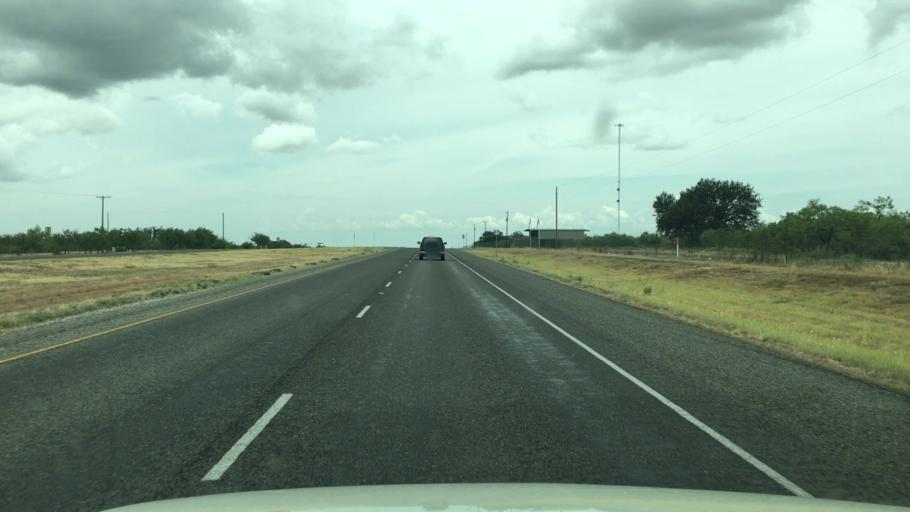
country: US
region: Texas
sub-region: Concho County
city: Eden
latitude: 31.2239
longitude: -99.9745
